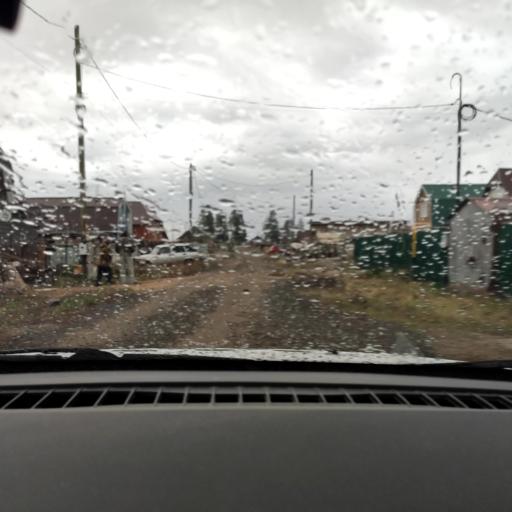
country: RU
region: Perm
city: Kultayevo
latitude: 57.8949
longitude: 55.9565
